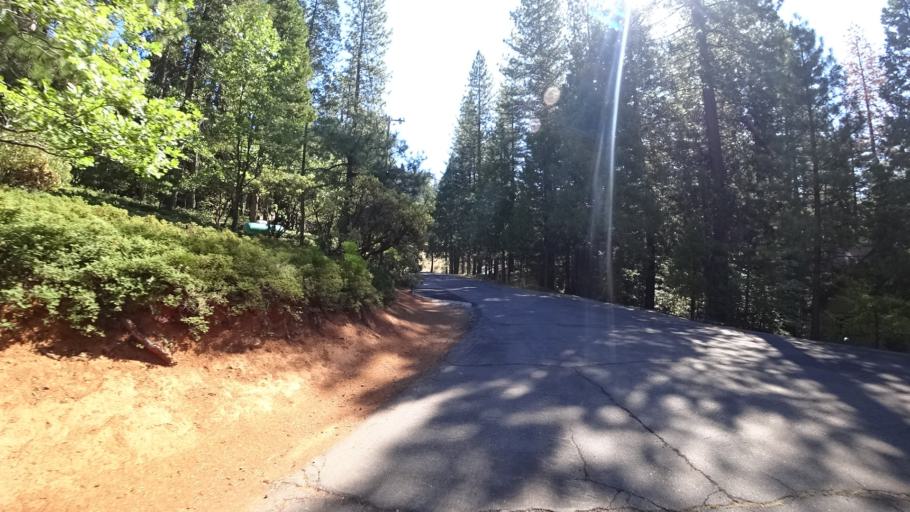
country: US
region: California
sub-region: Calaveras County
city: Arnold
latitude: 38.2451
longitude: -120.3728
